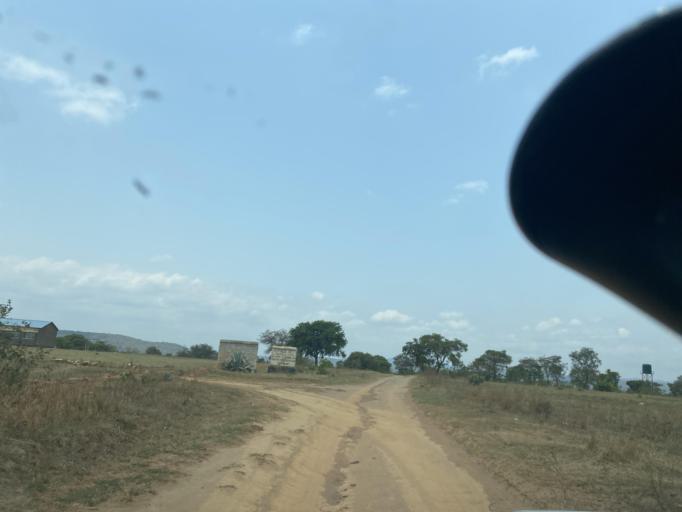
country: ZM
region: Lusaka
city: Chongwe
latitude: -15.5162
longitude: 28.8764
